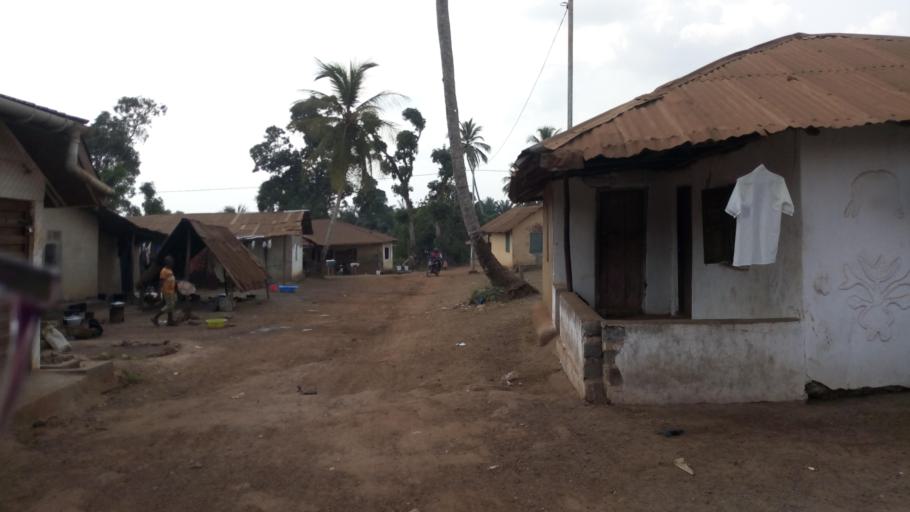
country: SL
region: Southern Province
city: Mogbwemo
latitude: 7.7868
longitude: -12.2976
